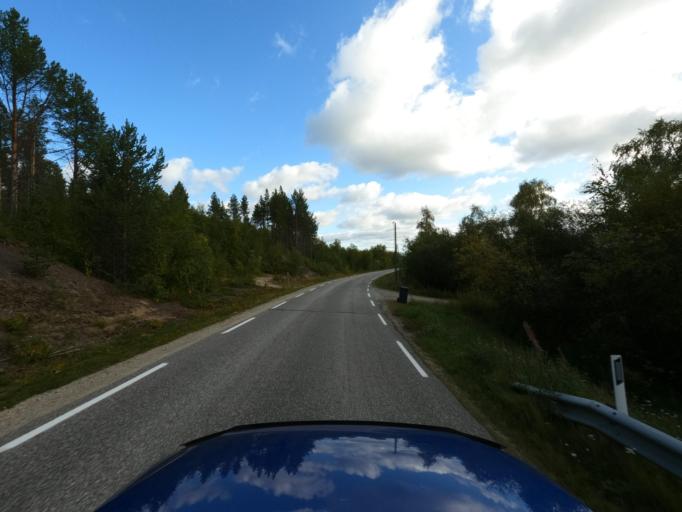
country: NO
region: Finnmark Fylke
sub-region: Karasjok
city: Karasjohka
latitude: 69.4567
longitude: 25.4054
